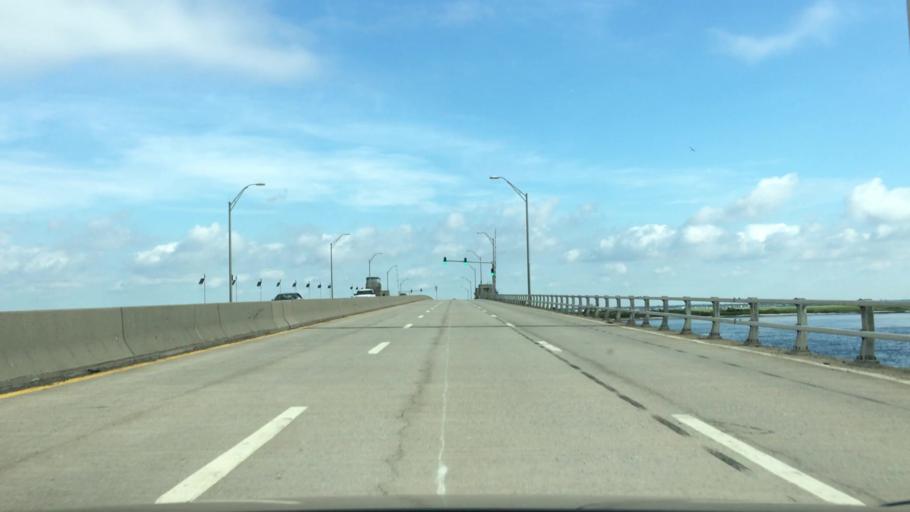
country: US
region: New York
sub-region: Nassau County
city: Point Lookout
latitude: 40.5972
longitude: -73.5426
